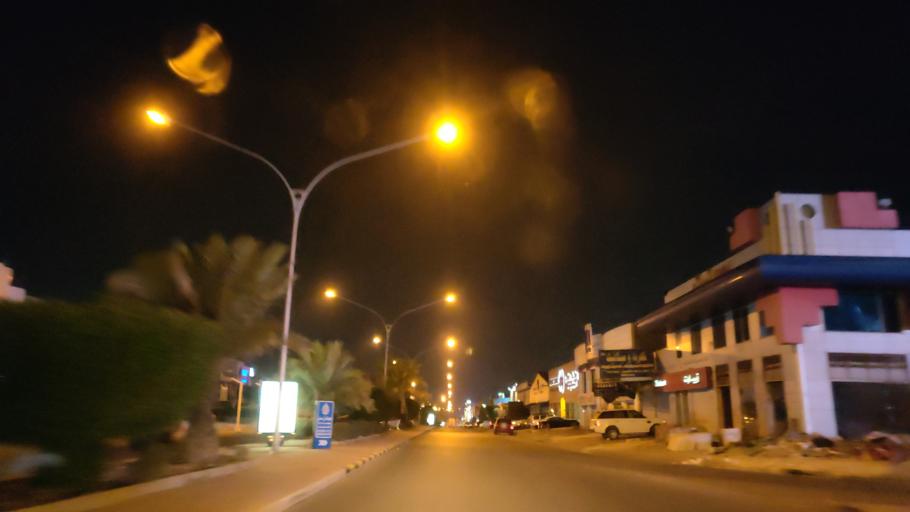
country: KW
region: Al Asimah
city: Ar Rabiyah
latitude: 29.3073
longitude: 47.9357
